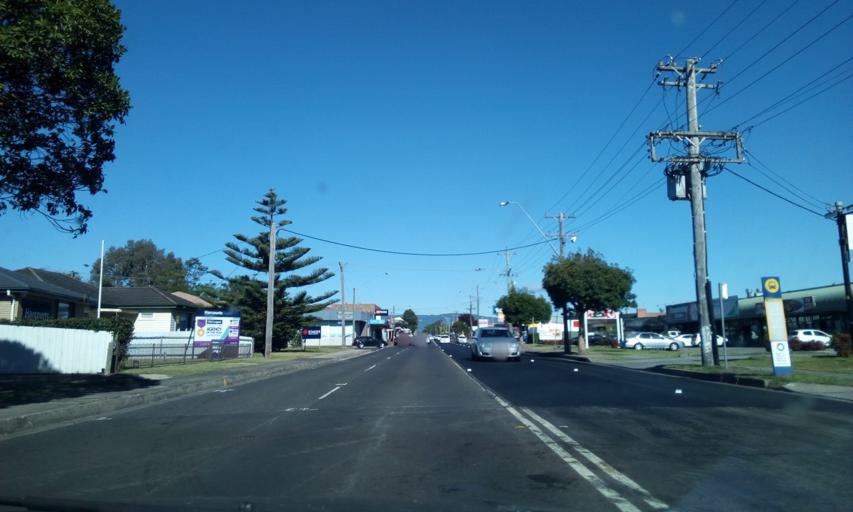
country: AU
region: New South Wales
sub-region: Wollongong
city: Dapto
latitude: -34.4912
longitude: 150.7966
